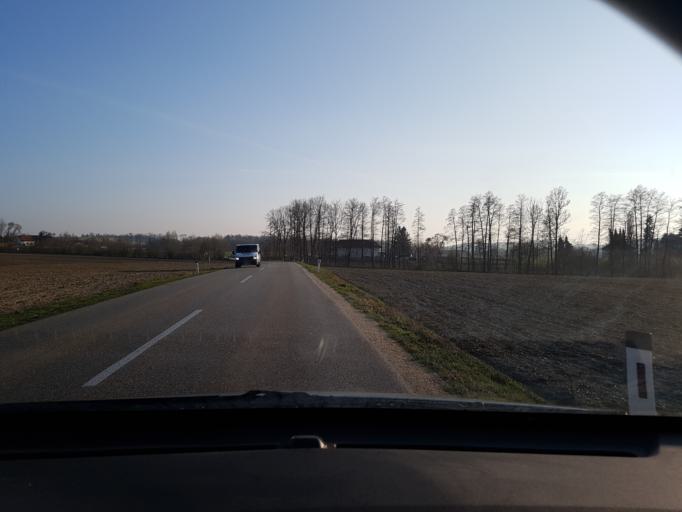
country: AT
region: Upper Austria
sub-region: Politischer Bezirk Linz-Land
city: Ansfelden
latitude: 48.1611
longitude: 14.2504
